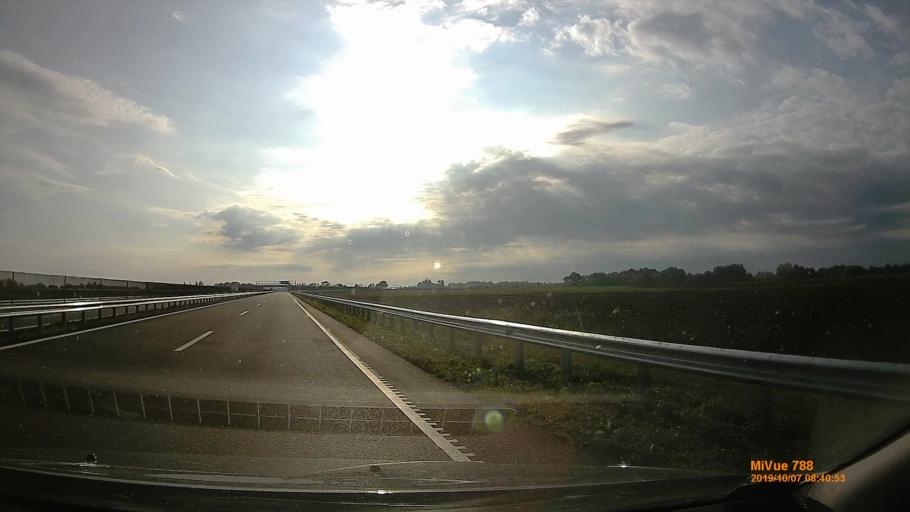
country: HU
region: Bekes
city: Bekesszentandras
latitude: 46.8217
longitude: 20.5058
